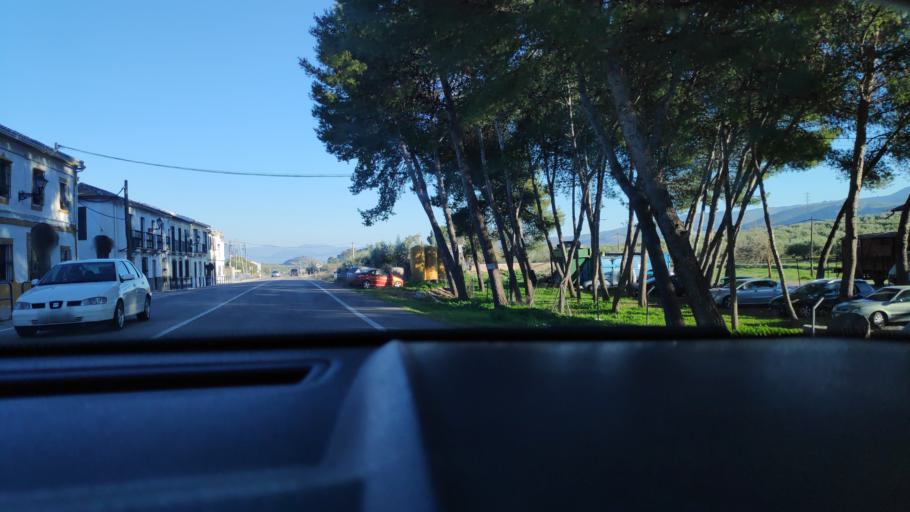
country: ES
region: Andalusia
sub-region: Province of Cordoba
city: Luque
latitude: 37.5732
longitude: -4.2617
